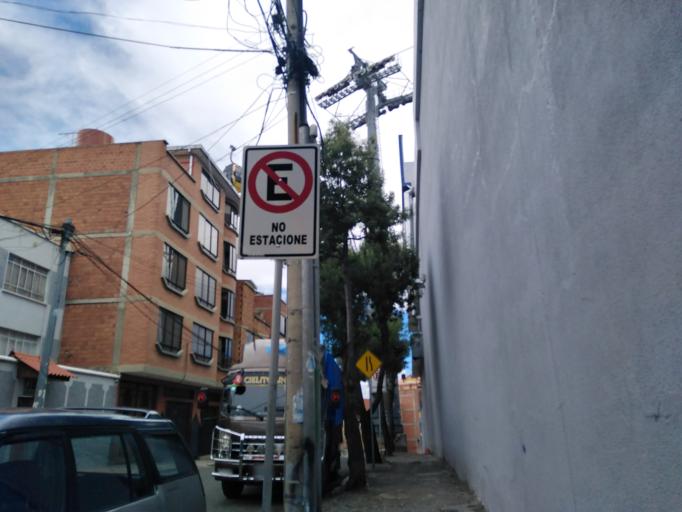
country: BO
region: La Paz
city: La Paz
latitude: -16.5149
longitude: -68.1382
